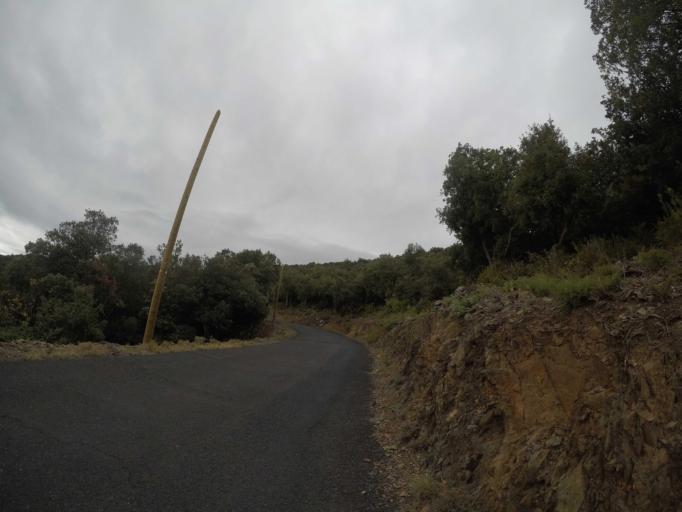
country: FR
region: Languedoc-Roussillon
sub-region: Departement des Pyrenees-Orientales
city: Ille-sur-Tet
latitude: 42.6256
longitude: 2.6185
